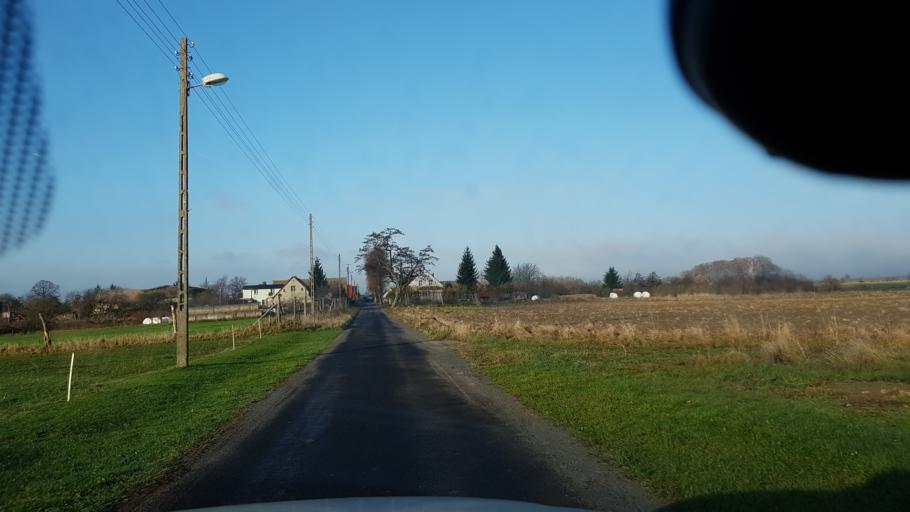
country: PL
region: West Pomeranian Voivodeship
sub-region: Powiat stargardzki
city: Dobrzany
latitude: 53.4032
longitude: 15.4377
